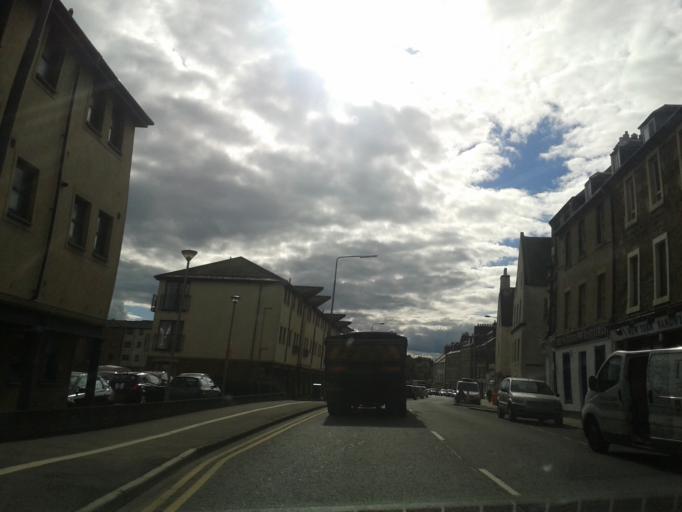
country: GB
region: Scotland
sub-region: Fife
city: Kirkcaldy
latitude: 56.1162
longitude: -3.1516
